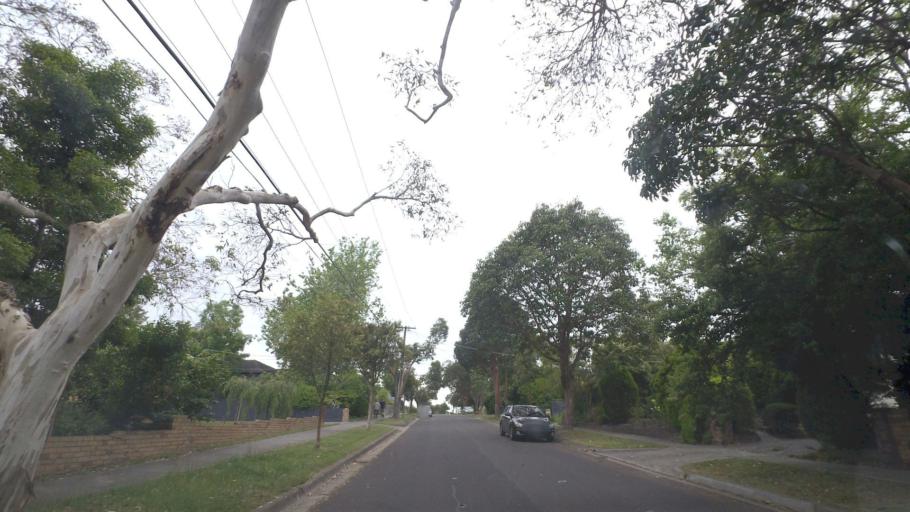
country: AU
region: Victoria
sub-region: Maroondah
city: Croydon North
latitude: -37.7917
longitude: 145.3010
